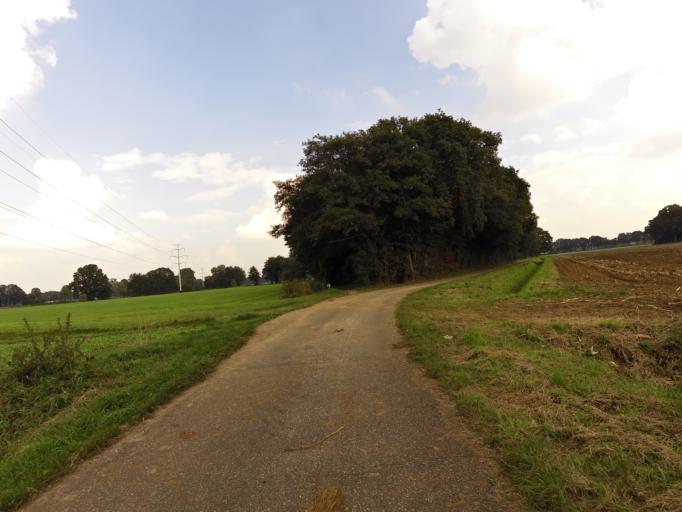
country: NL
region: Gelderland
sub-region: Gemeente Aalten
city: Aalten
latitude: 51.9355
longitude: 6.5463
